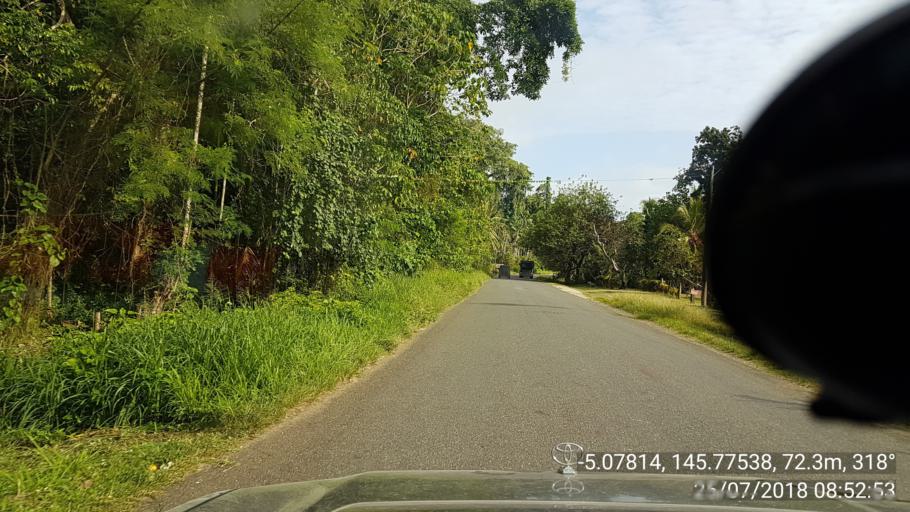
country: PG
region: Madang
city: Madang
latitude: -5.0782
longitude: 145.7755
